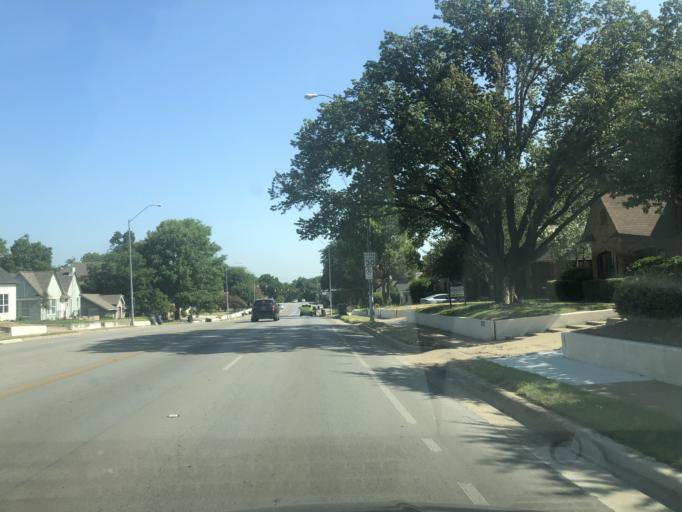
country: US
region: Texas
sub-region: Tarrant County
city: Fort Worth
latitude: 32.7140
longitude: -97.3603
